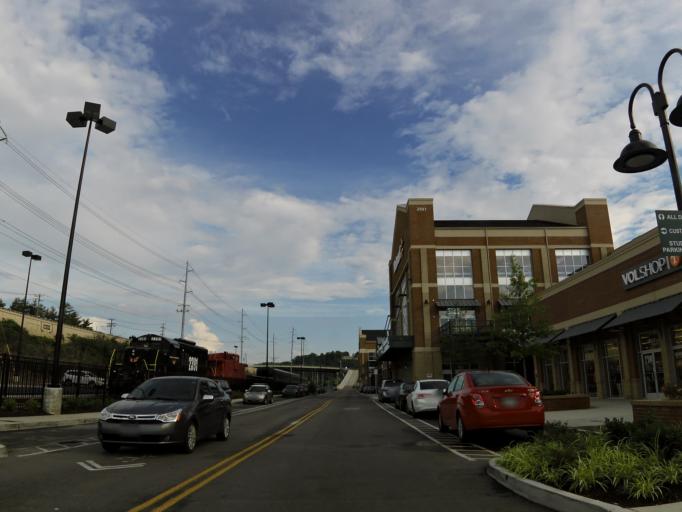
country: US
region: Tennessee
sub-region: Knox County
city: Knoxville
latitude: 35.9517
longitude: -83.9401
